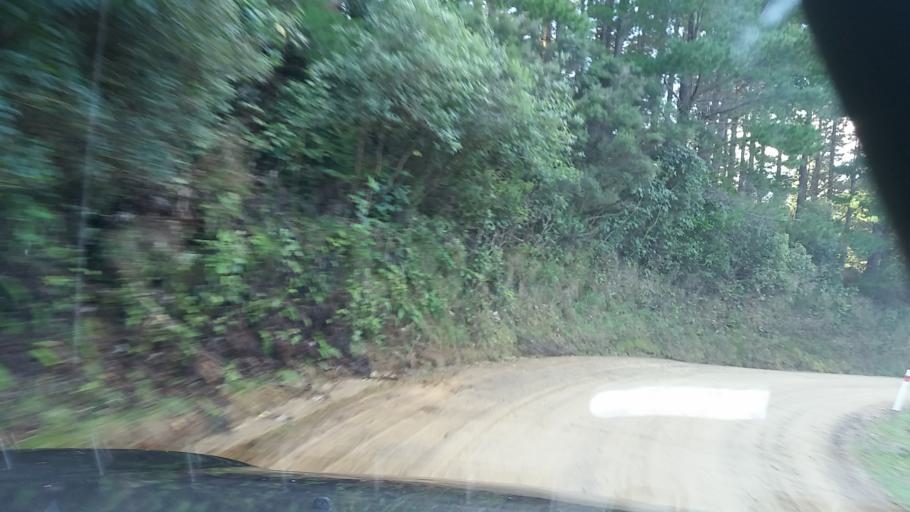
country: NZ
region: Marlborough
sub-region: Marlborough District
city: Picton
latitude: -40.9867
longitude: 173.8176
